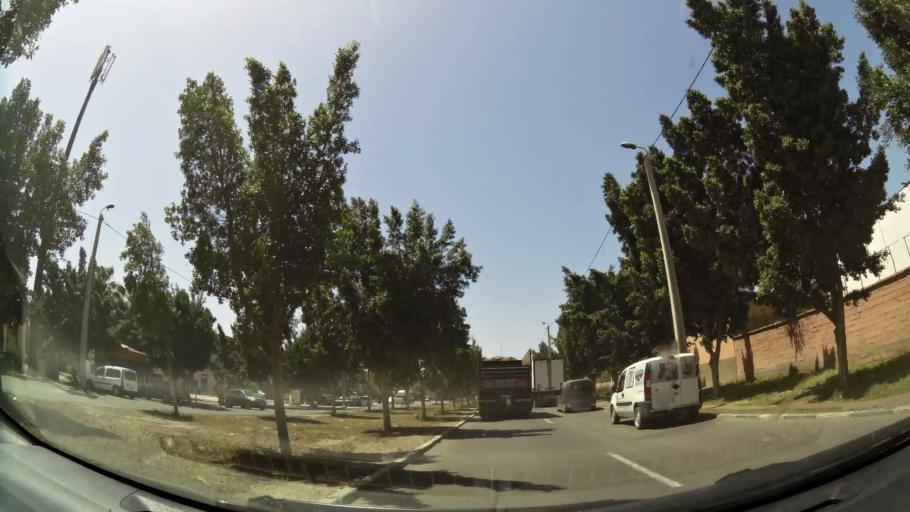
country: MA
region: Souss-Massa-Draa
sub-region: Inezgane-Ait Mellou
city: Inezgane
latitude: 30.3319
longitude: -9.4921
